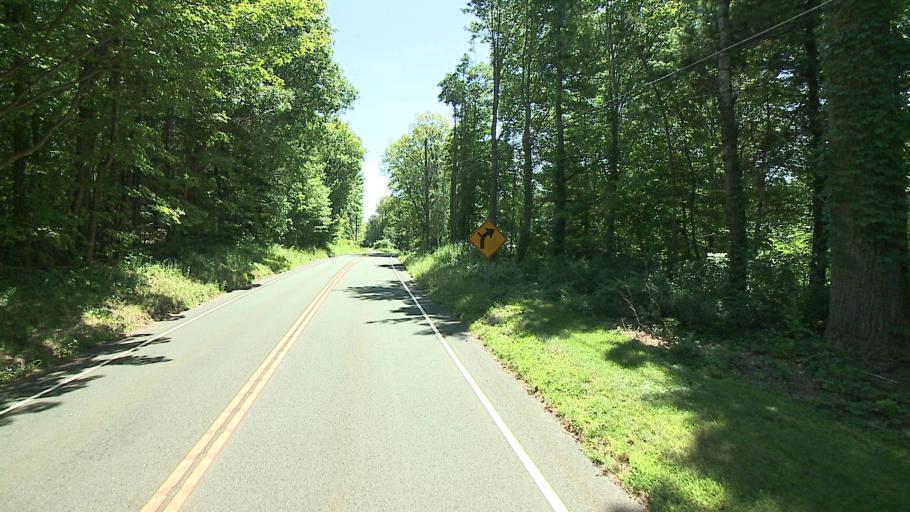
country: US
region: Connecticut
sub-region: Litchfield County
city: New Hartford Center
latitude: 41.9381
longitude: -72.9706
